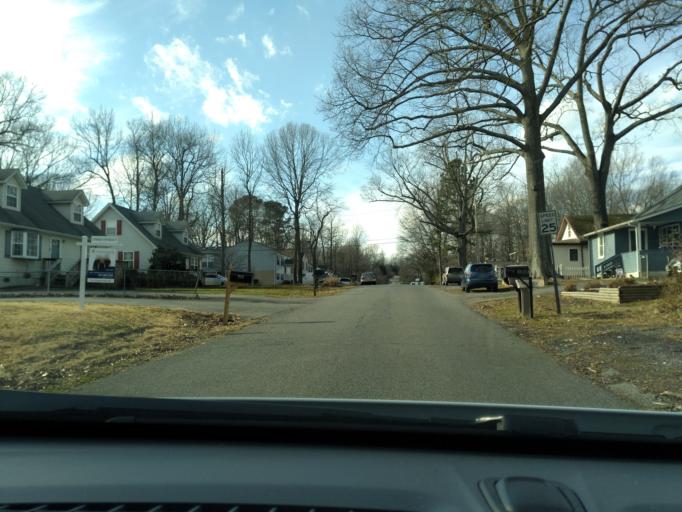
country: US
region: Maryland
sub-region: Calvert County
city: North Beach
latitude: 38.7100
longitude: -76.5377
